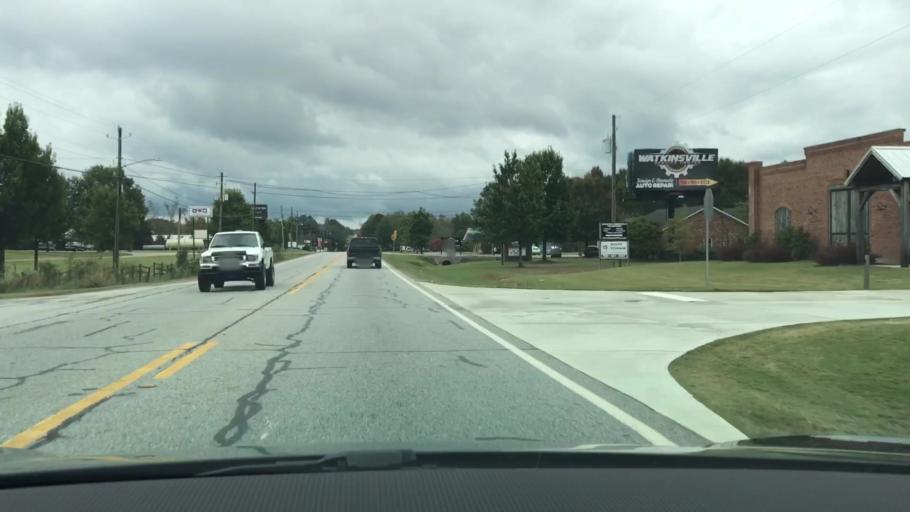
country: US
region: Georgia
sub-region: Oconee County
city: Watkinsville
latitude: 33.8546
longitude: -83.4006
